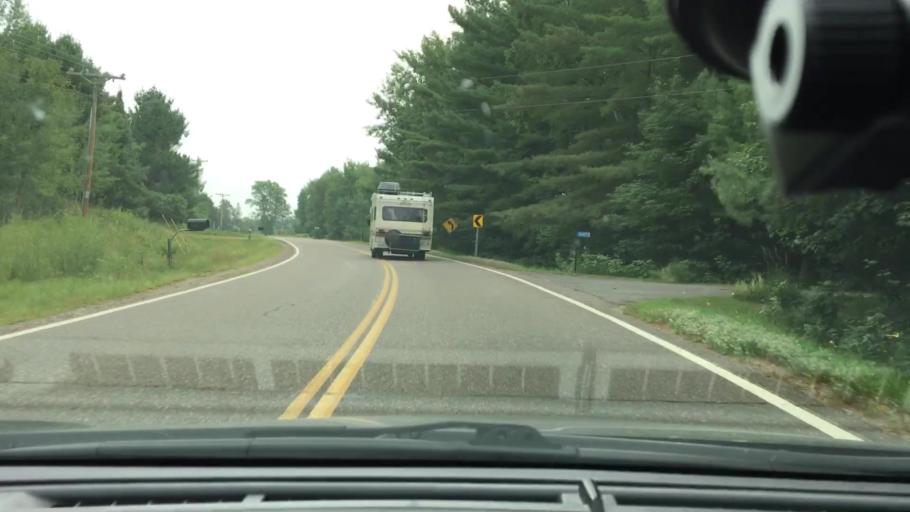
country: US
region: Minnesota
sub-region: Aitkin County
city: Aitkin
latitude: 46.4015
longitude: -93.7732
